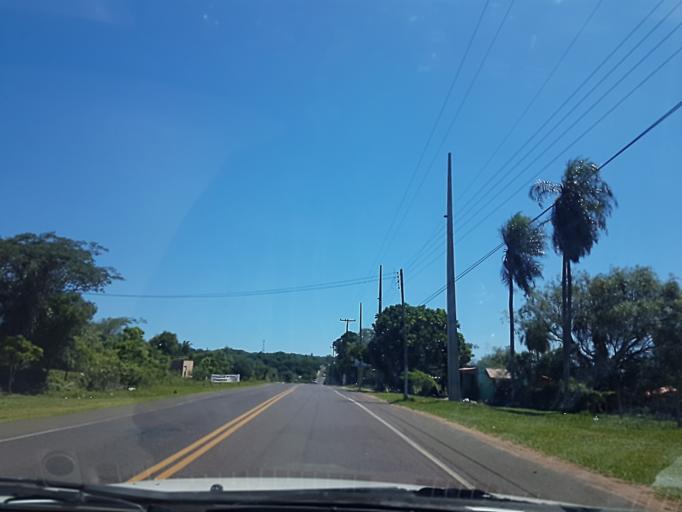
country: PY
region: Cordillera
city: Altos
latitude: -25.2548
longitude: -57.2429
